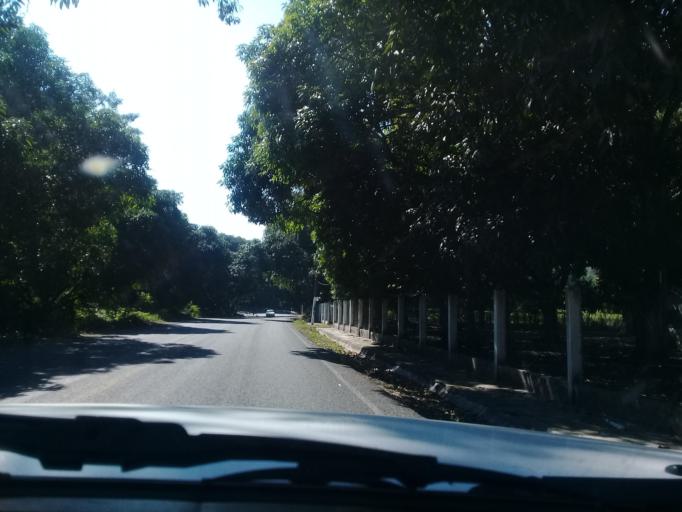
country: MX
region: Veracruz
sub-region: Emiliano Zapata
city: Plan del Rio
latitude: 19.4204
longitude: -96.6163
